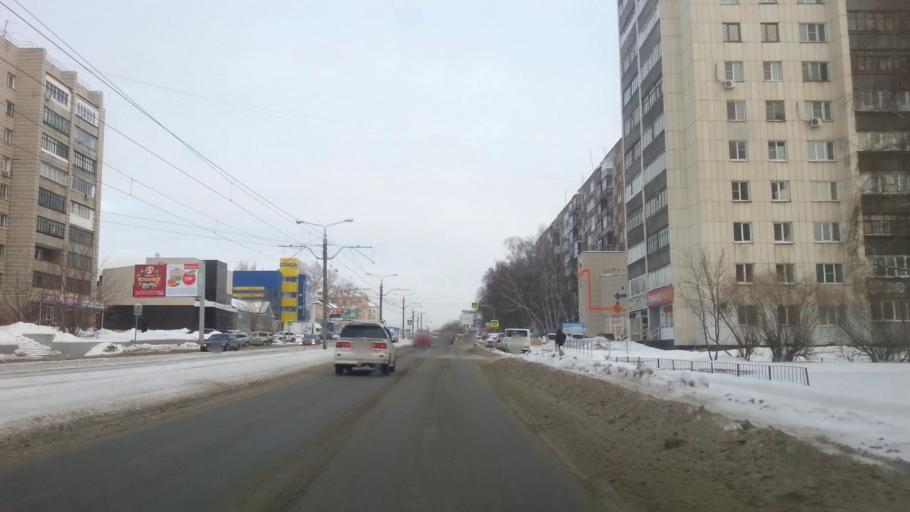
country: RU
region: Altai Krai
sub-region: Gorod Barnaulskiy
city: Barnaul
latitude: 53.3715
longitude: 83.7454
